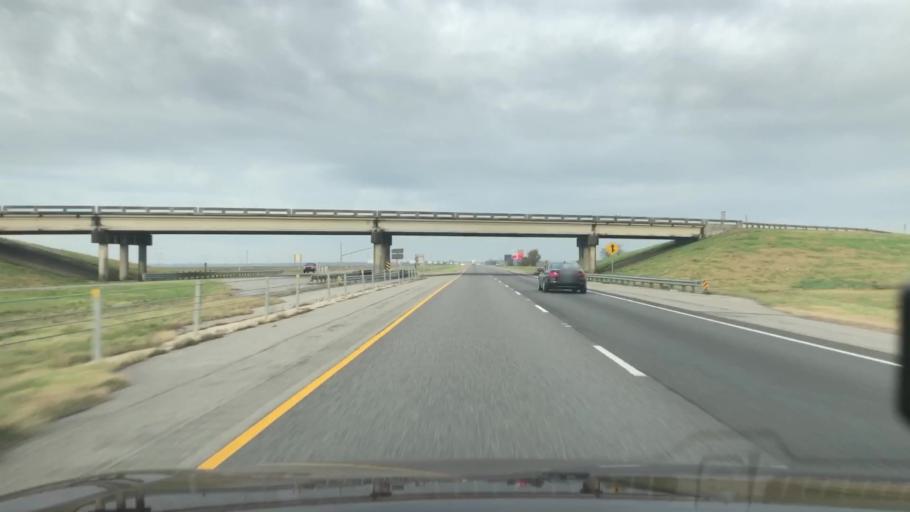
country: US
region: Mississippi
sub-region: Warren County
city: Vicksburg
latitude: 32.3227
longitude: -90.9581
